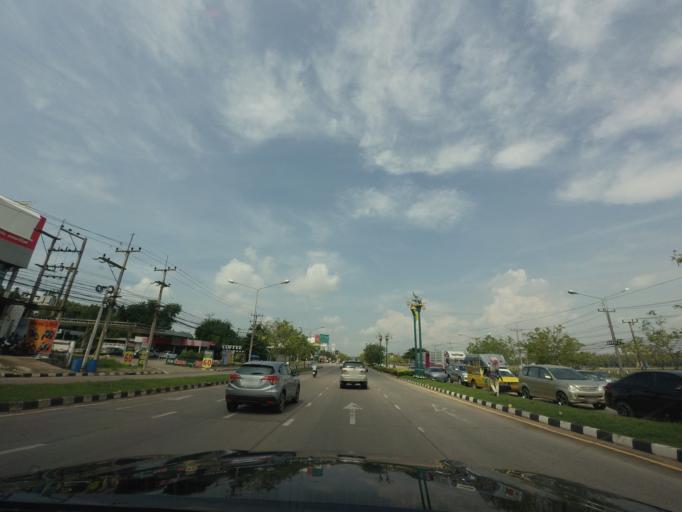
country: TH
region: Khon Kaen
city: Khon Kaen
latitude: 16.4410
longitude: 102.8187
